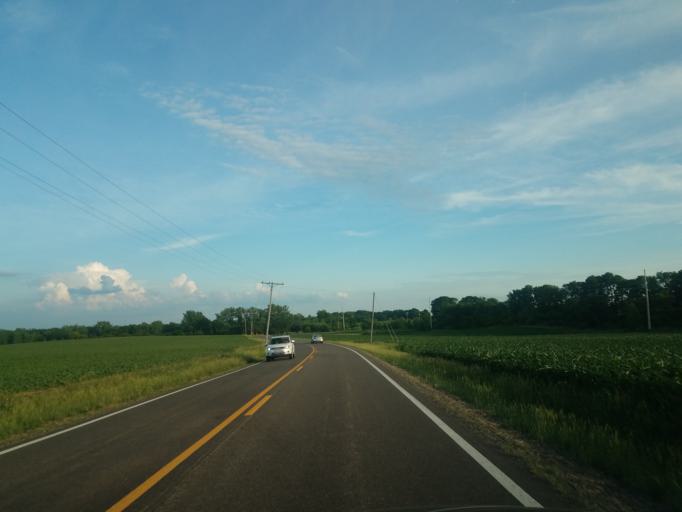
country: US
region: Illinois
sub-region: McLean County
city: Bloomington
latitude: 40.4470
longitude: -88.9657
